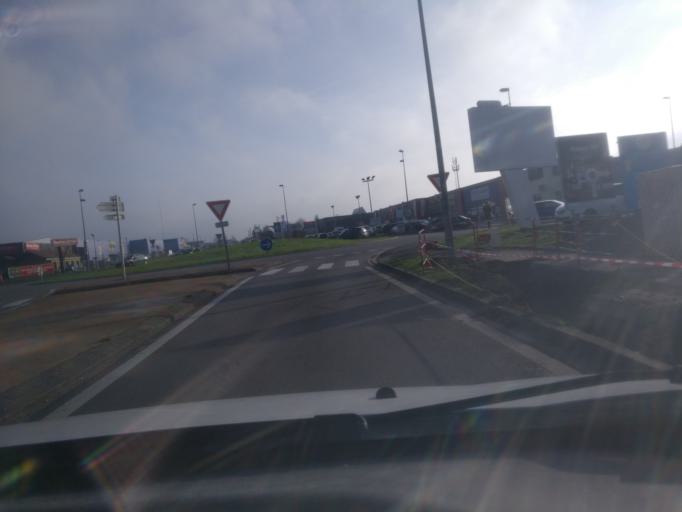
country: FR
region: Pays de la Loire
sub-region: Departement de la Loire-Atlantique
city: Vertou
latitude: 47.1861
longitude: -1.4640
